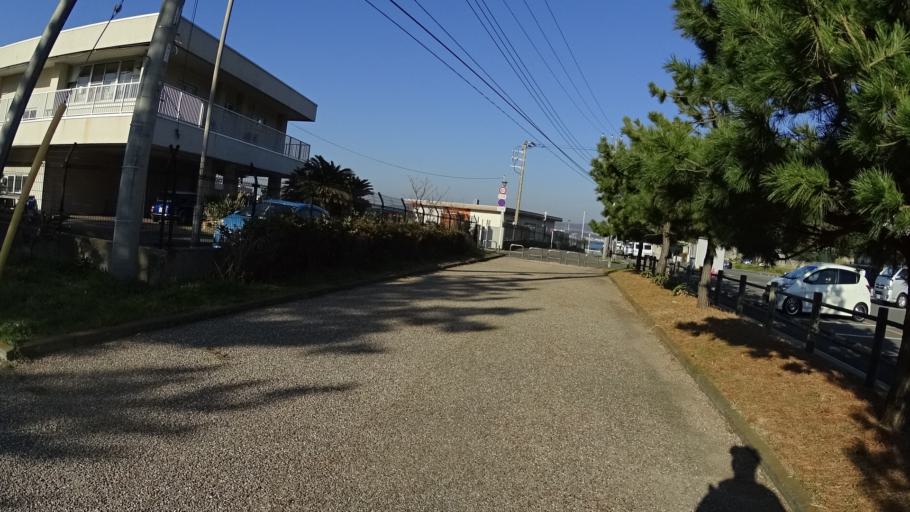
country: JP
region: Kanagawa
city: Miura
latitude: 35.1955
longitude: 139.6012
